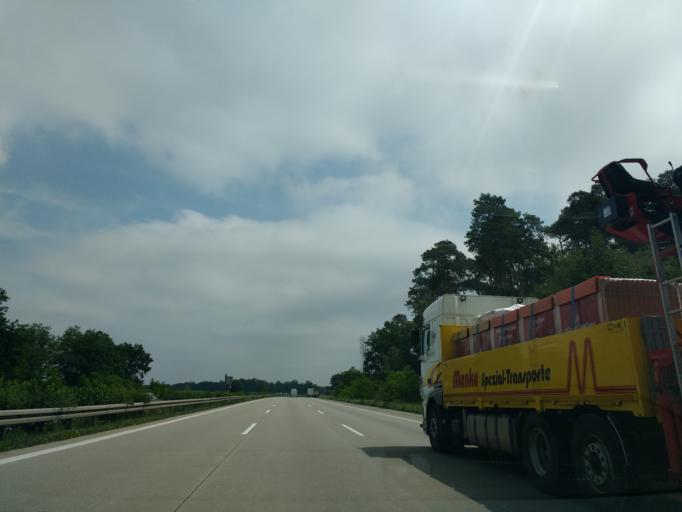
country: DE
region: Saxony-Anhalt
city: Mockern
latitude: 52.2360
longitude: 11.9762
